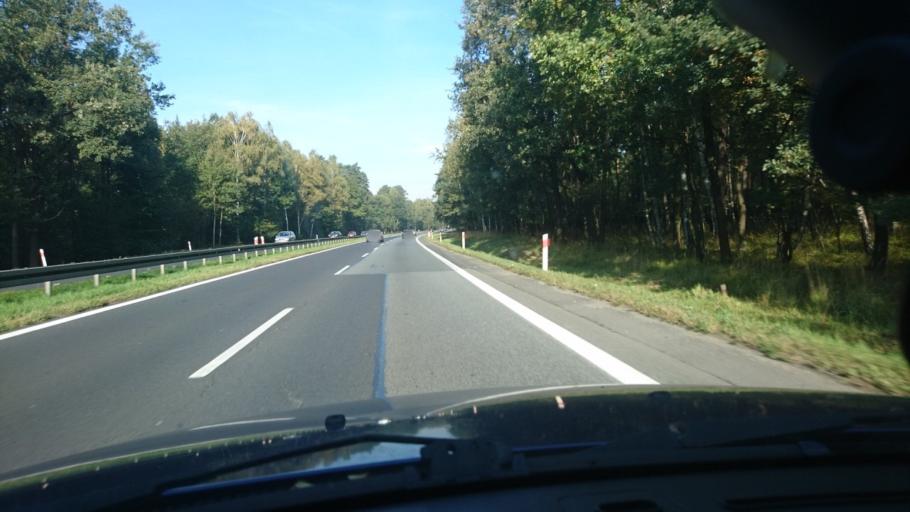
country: PL
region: Silesian Voivodeship
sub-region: Powiat pszczynski
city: Piasek
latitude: 50.0216
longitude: 18.9443
